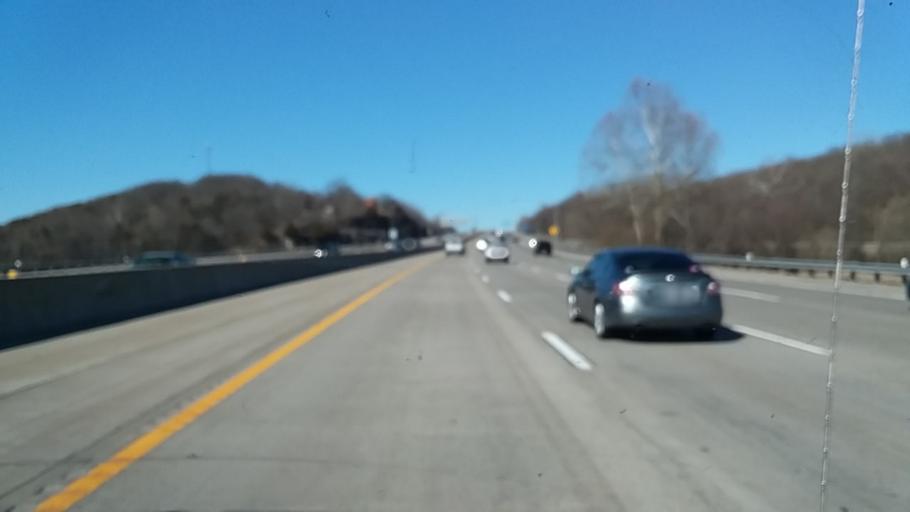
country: US
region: Missouri
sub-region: Jefferson County
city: Barnhart
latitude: 38.3501
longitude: -90.3949
